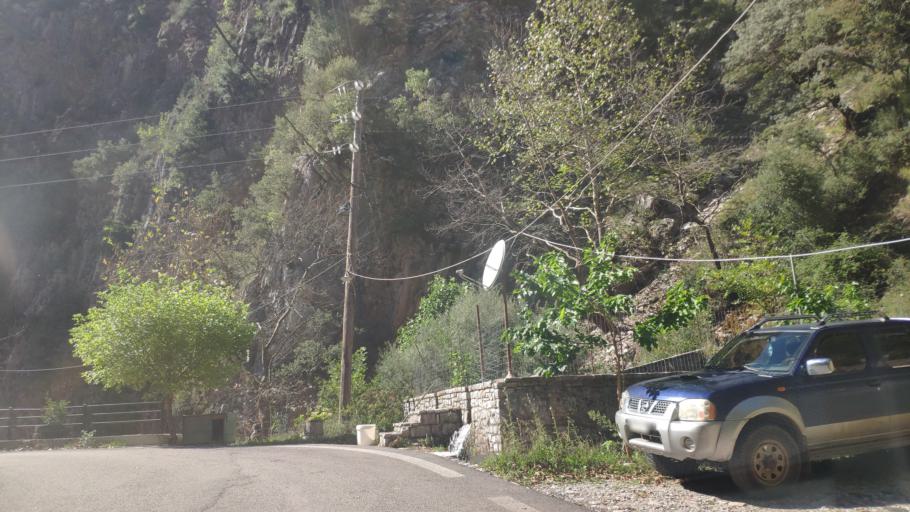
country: GR
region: Central Greece
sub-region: Nomos Evrytanias
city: Kerasochori
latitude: 39.1369
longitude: 21.6383
